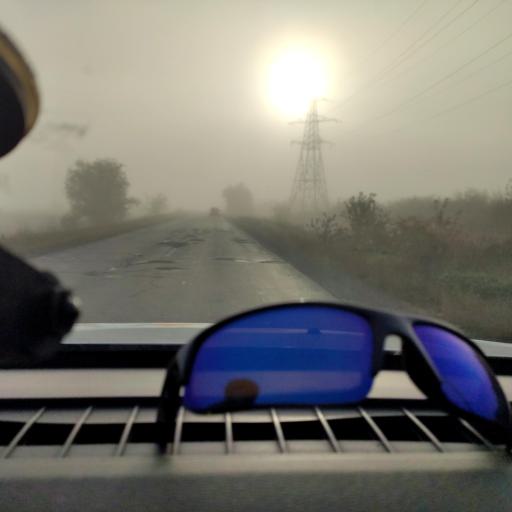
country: RU
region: Samara
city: Chapayevsk
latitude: 53.0012
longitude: 49.7586
